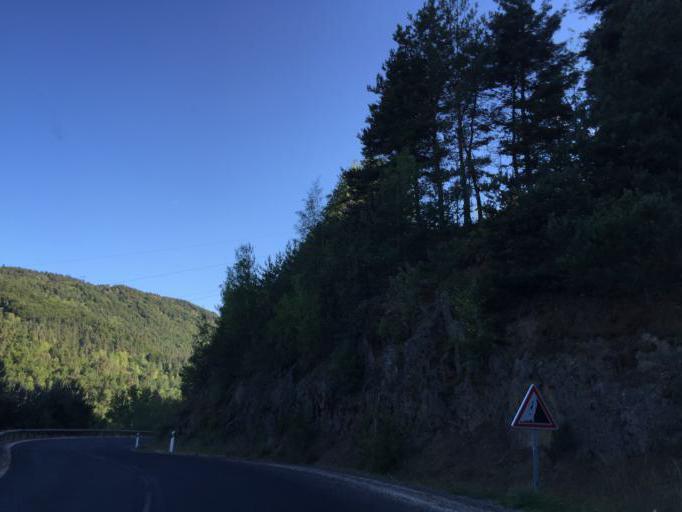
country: FR
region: Auvergne
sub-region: Departement de la Haute-Loire
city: Saugues
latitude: 44.9629
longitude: 3.6271
